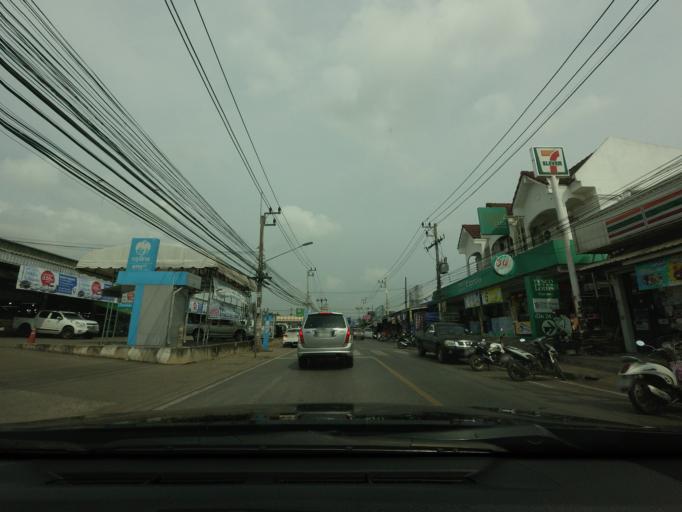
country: TH
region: Surat Thani
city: Surat Thani
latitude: 9.1073
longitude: 99.3079
